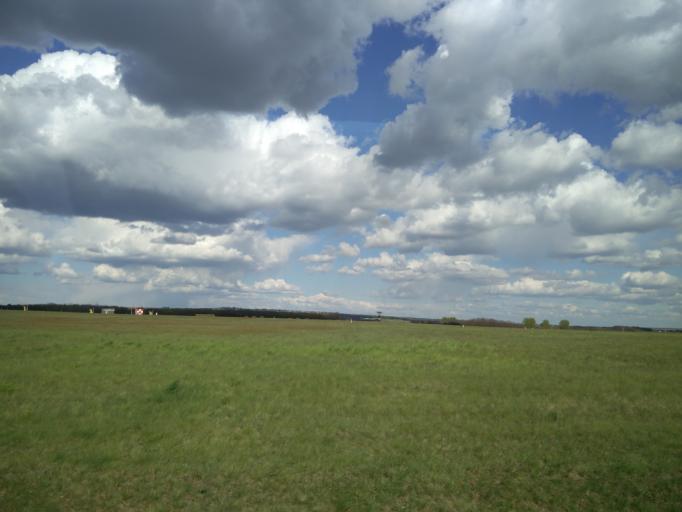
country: HU
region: Budapest
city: Budapest XVII. keruelet
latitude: 47.4459
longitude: 19.2506
